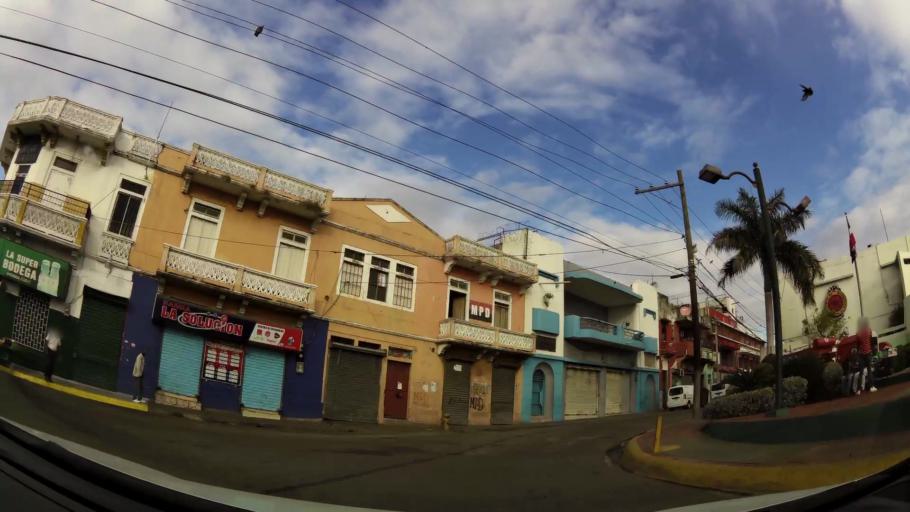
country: DO
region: Nacional
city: Ciudad Nueva
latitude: 18.4729
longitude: -69.8921
